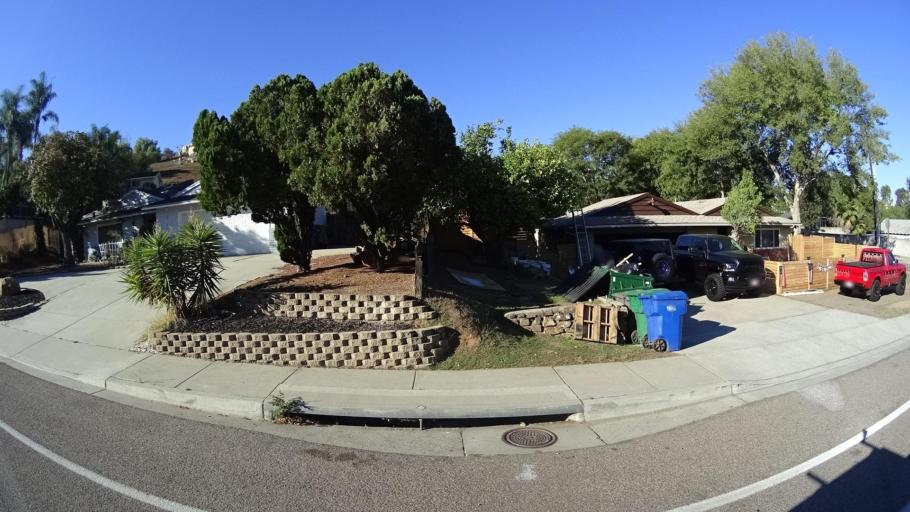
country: US
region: California
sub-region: San Diego County
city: Winter Gardens
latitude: 32.8349
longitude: -116.9071
